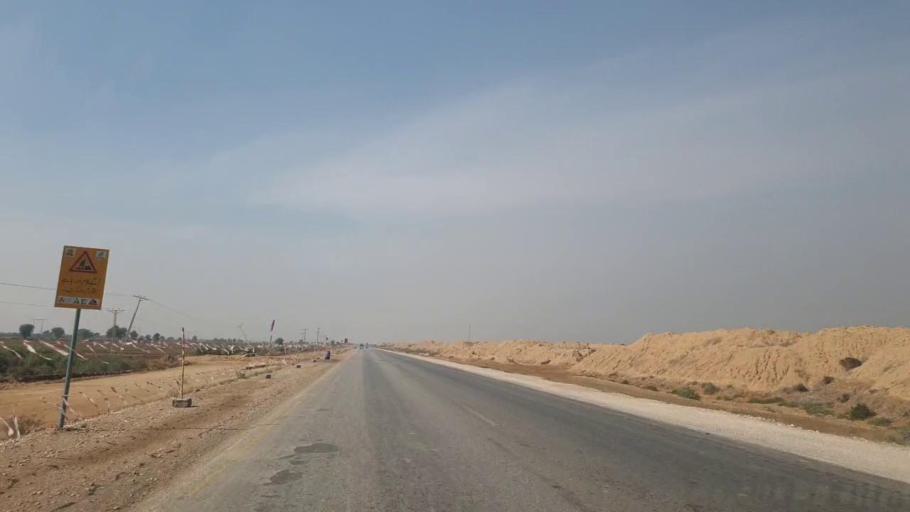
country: PK
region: Sindh
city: Sann
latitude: 26.0058
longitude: 68.1552
